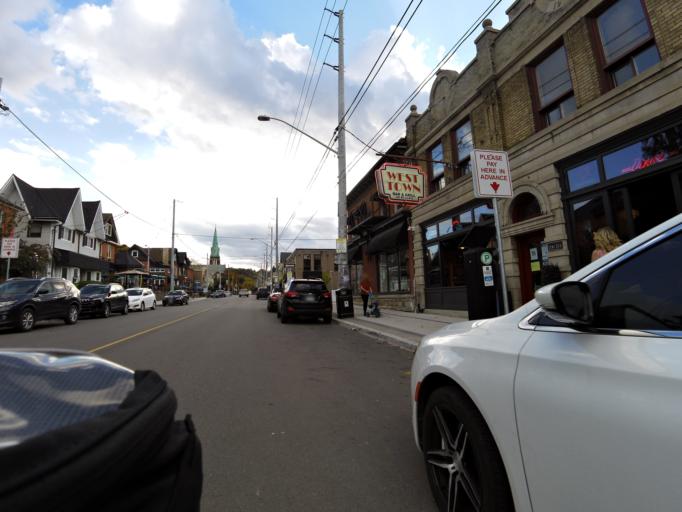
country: CA
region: Ontario
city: Hamilton
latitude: 43.2546
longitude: -79.8861
